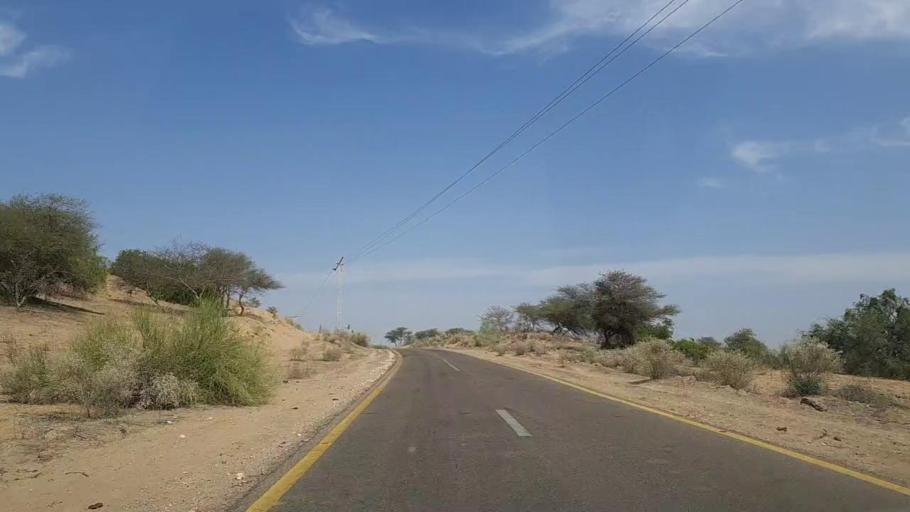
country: PK
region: Sindh
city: Mithi
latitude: 24.8412
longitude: 69.8355
